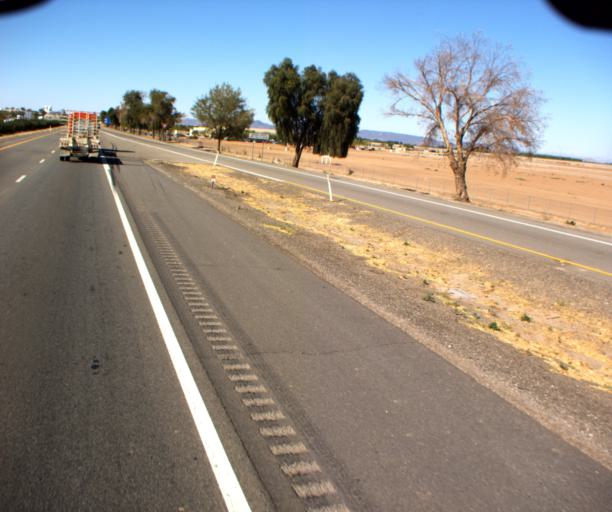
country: US
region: Arizona
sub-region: Yuma County
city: Yuma
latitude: 32.7111
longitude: -114.6110
